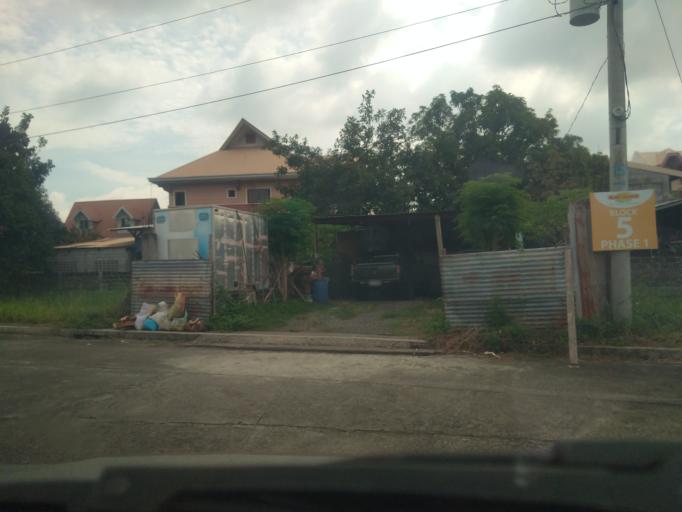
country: PH
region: Central Luzon
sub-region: Province of Pampanga
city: Santo Domingo
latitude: 15.0025
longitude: 120.7257
